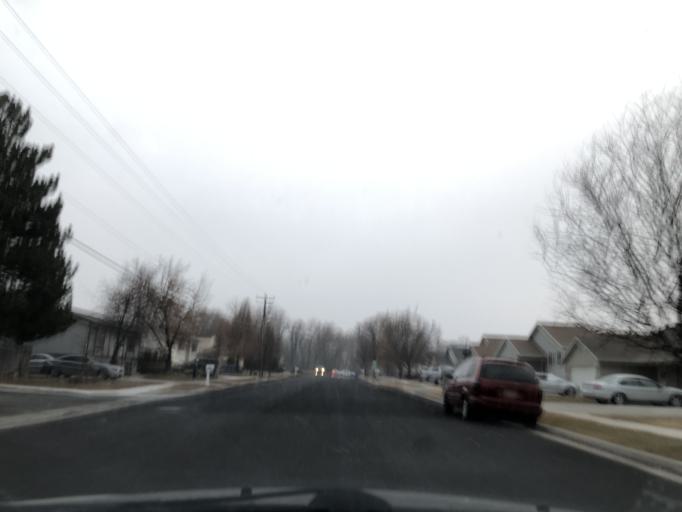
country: US
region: Utah
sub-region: Cache County
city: Logan
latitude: 41.7170
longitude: -111.8426
